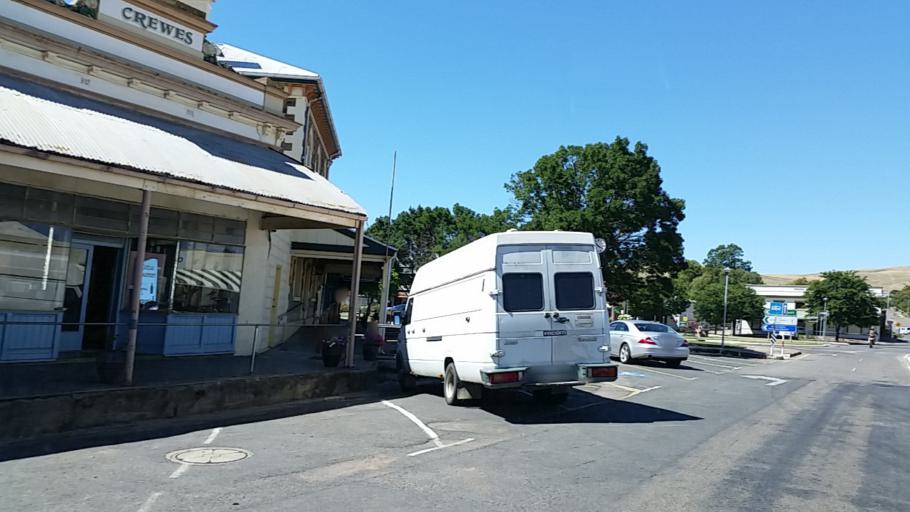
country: AU
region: South Australia
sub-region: Clare and Gilbert Valleys
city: Clare
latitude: -33.6824
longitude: 138.9383
